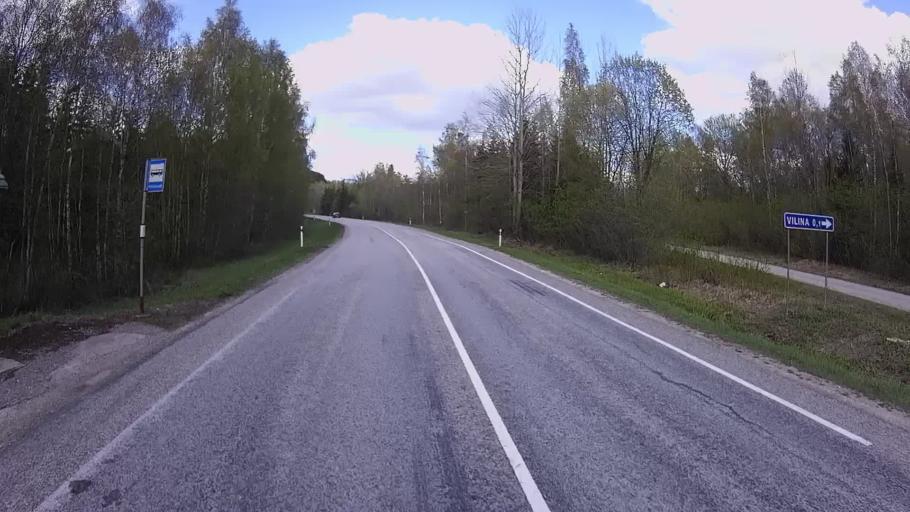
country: EE
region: Jogevamaa
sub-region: Jogeva linn
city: Jogeva
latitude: 58.7742
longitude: 26.4684
